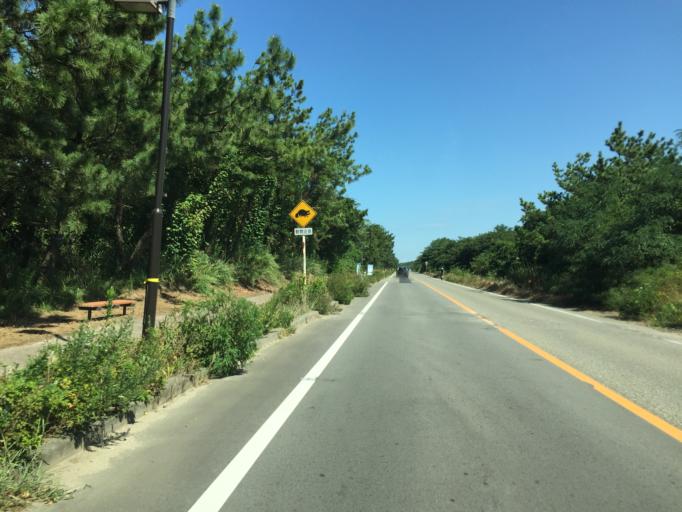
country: JP
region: Niigata
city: Niigata-shi
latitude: 37.9024
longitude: 138.9922
